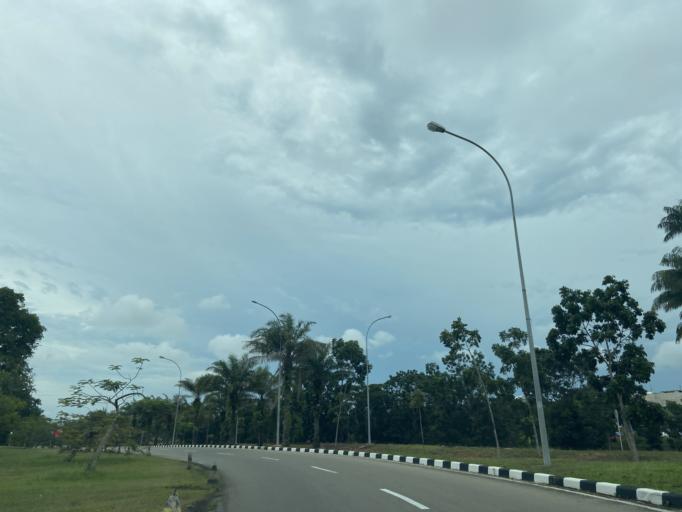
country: SG
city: Singapore
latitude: 1.1236
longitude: 104.1125
